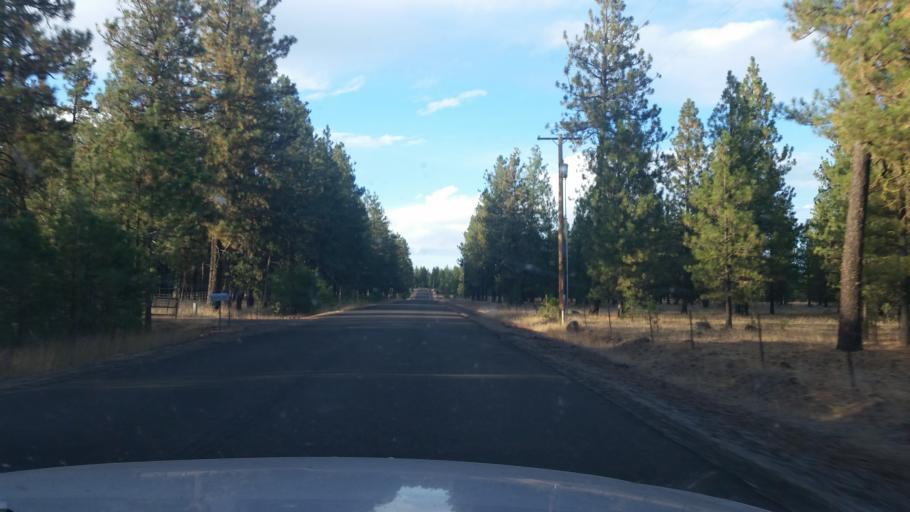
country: US
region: Washington
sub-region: Spokane County
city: Medical Lake
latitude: 47.4441
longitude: -117.7898
